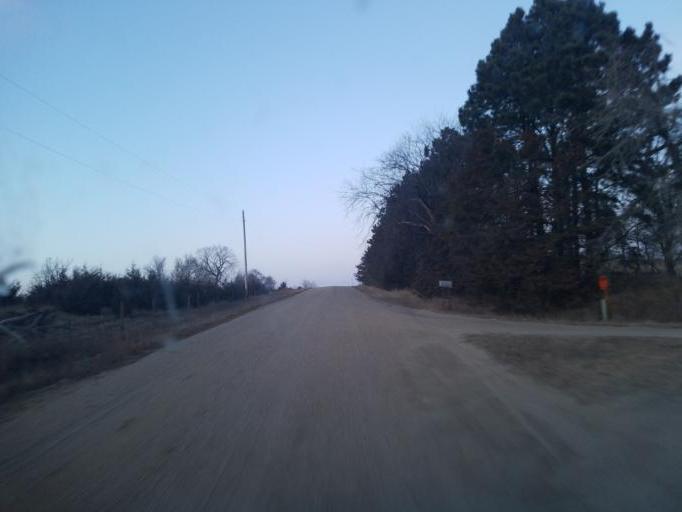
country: US
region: Nebraska
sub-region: Knox County
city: Center
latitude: 42.6189
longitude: -97.8378
